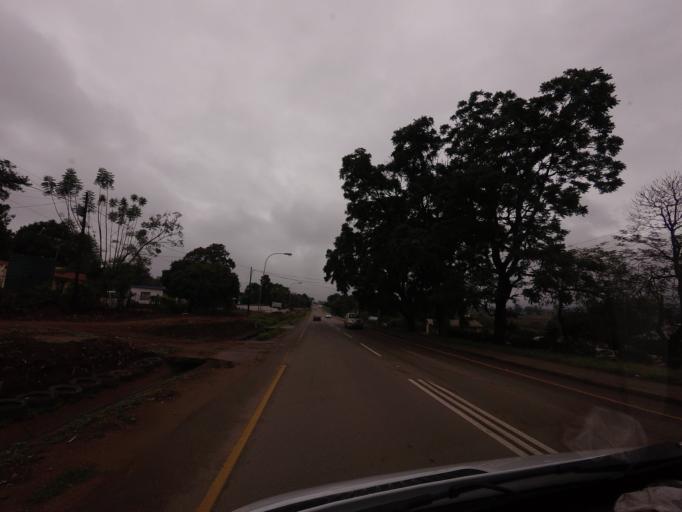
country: SZ
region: Manzini
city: Malkerns
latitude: -26.5275
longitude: 31.1910
